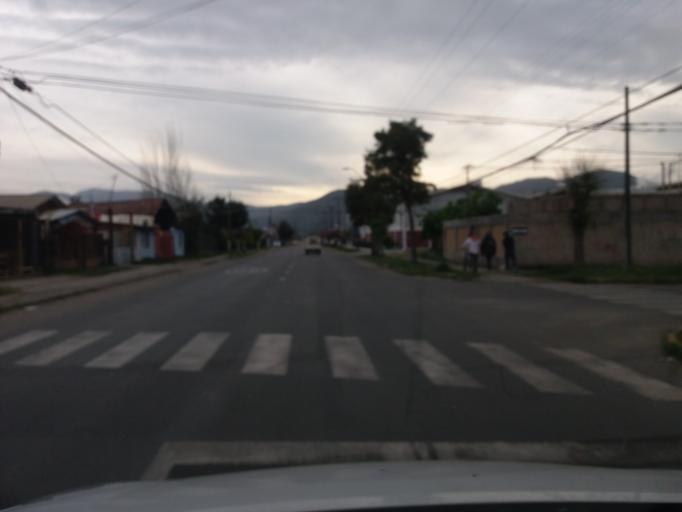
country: CL
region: Valparaiso
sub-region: Provincia de Quillota
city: Hacienda La Calera
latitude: -32.7788
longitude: -71.1864
